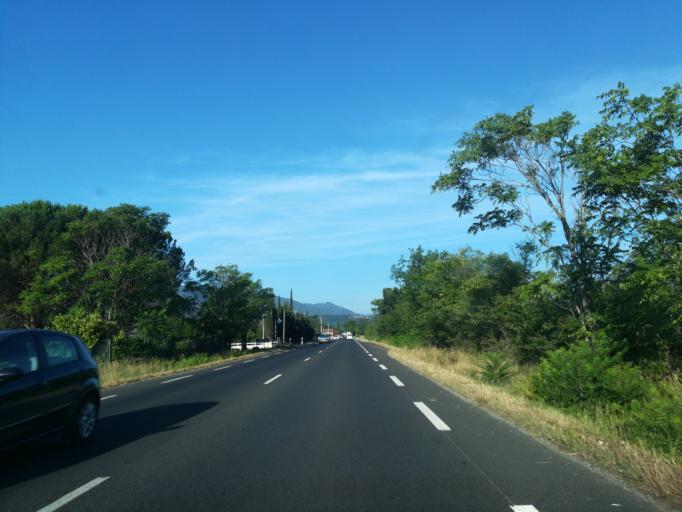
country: FR
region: Languedoc-Roussillon
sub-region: Departement des Pyrenees-Orientales
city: Sant Joan de Pladecorts
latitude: 42.5070
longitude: 2.7692
